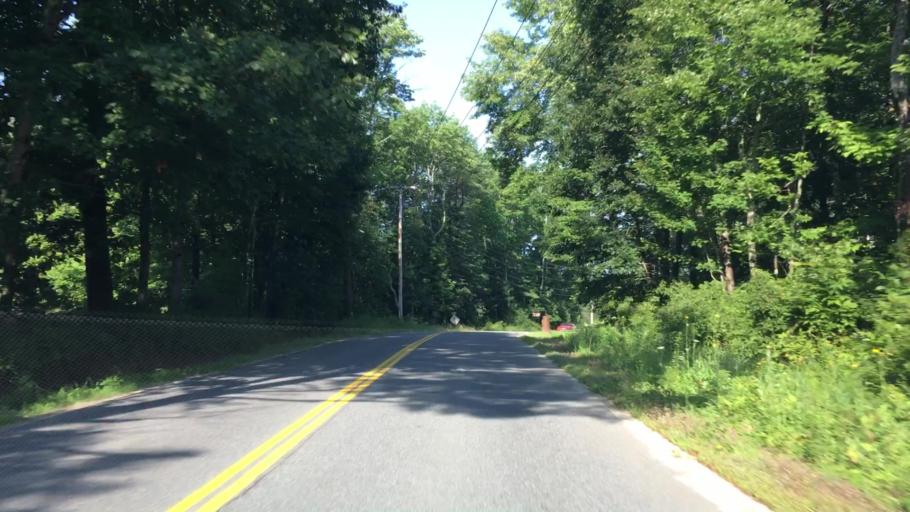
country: US
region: Maine
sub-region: Androscoggin County
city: Minot
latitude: 44.0432
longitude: -70.3220
